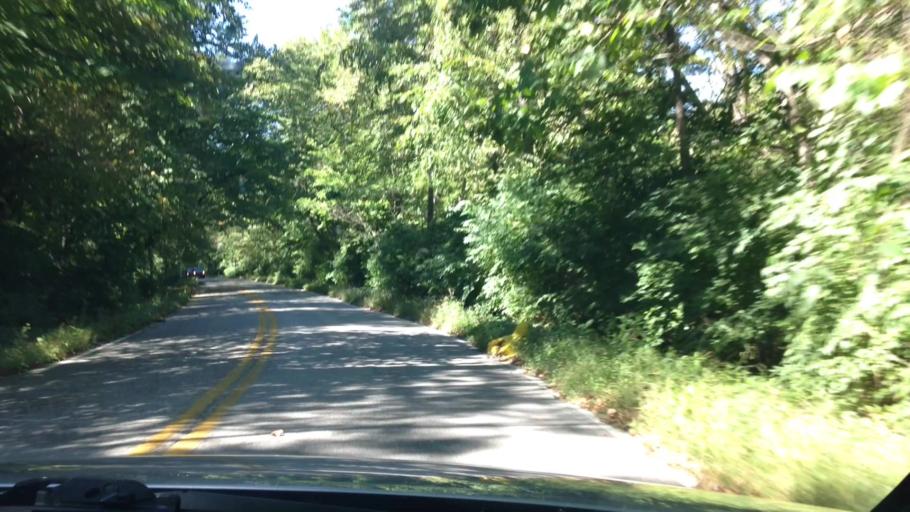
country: US
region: Missouri
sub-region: Jackson County
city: Raytown
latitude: 39.0040
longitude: -94.5143
